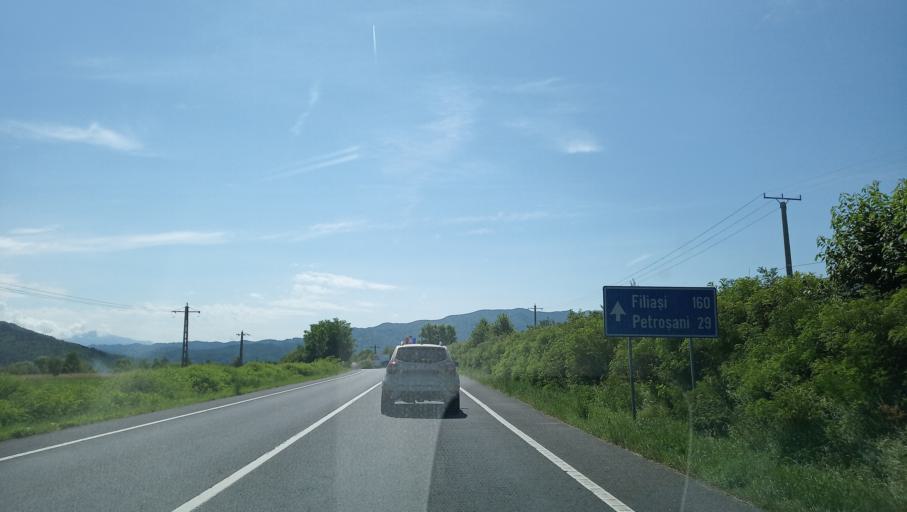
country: RO
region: Hunedoara
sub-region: Comuna Pui
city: Pui
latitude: 45.4968
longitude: 23.1163
